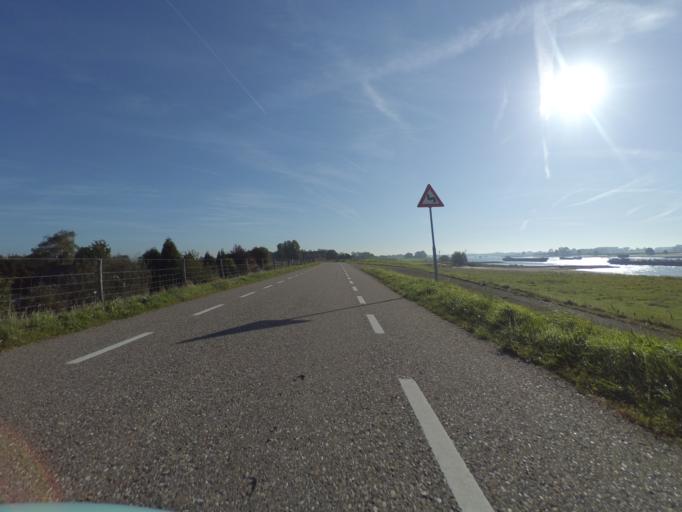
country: NL
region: Gelderland
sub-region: Gemeente Overbetuwe
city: Zetten
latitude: 51.8981
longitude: 5.6940
